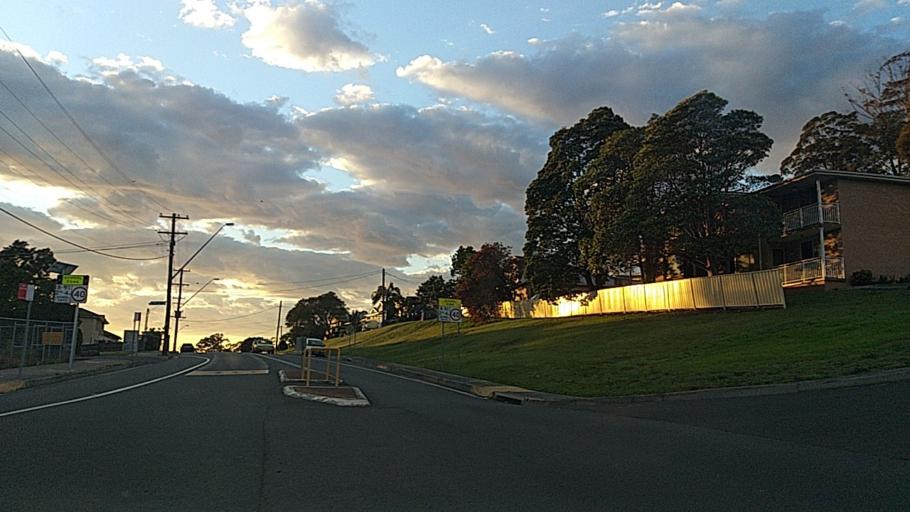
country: AU
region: New South Wales
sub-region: Wollongong
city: Koonawarra
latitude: -34.4910
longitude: 150.8132
